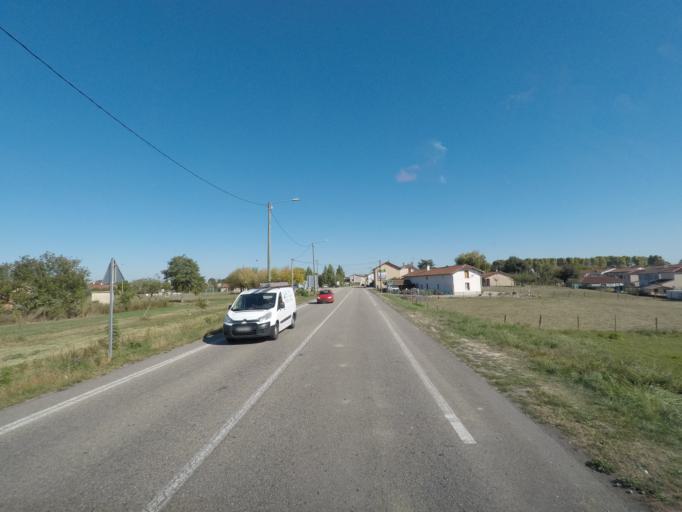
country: FR
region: Rhone-Alpes
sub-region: Departement de l'Ain
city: Servas
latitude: 46.1294
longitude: 5.1622
